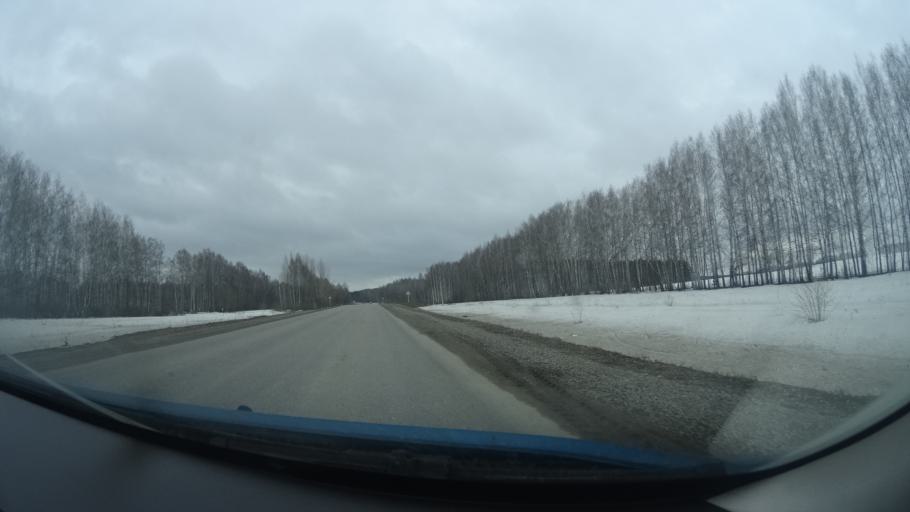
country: RU
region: Bashkortostan
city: Birsk
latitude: 55.3407
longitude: 55.5929
